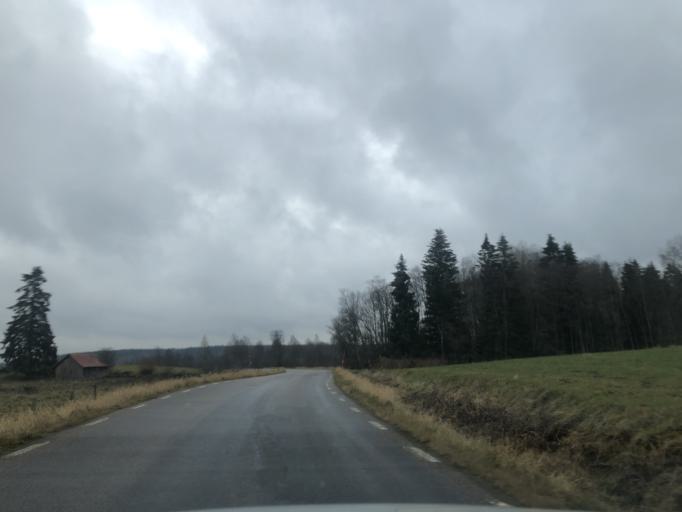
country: SE
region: Vaestra Goetaland
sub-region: Ulricehamns Kommun
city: Ulricehamn
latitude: 57.8913
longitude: 13.5101
